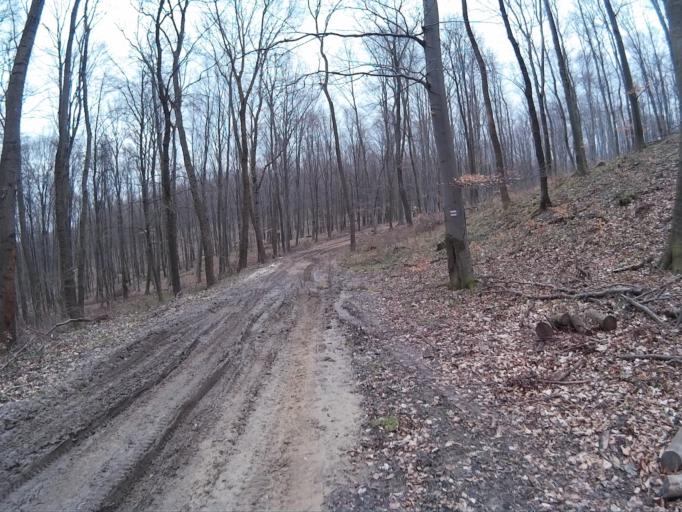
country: HU
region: Veszprem
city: Zirc
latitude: 47.1828
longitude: 17.8782
